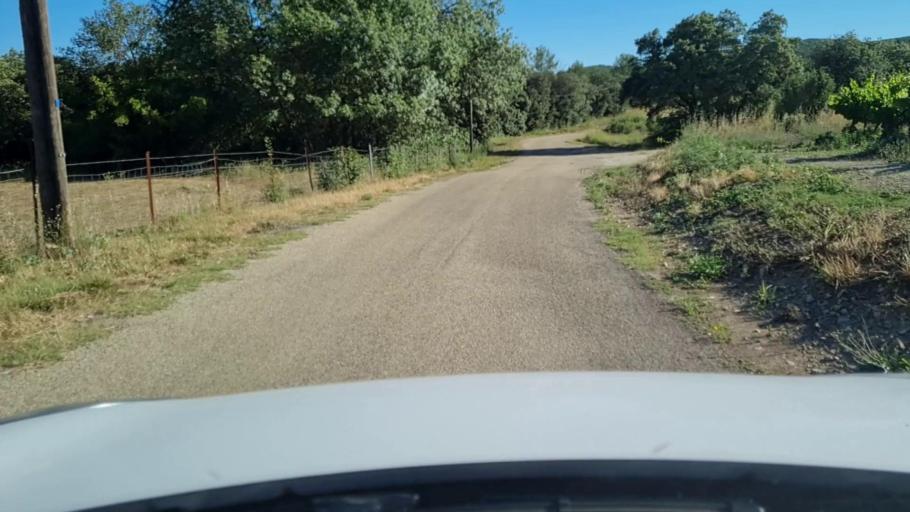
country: FR
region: Languedoc-Roussillon
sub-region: Departement du Gard
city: Villevieille
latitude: 43.8420
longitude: 4.0766
